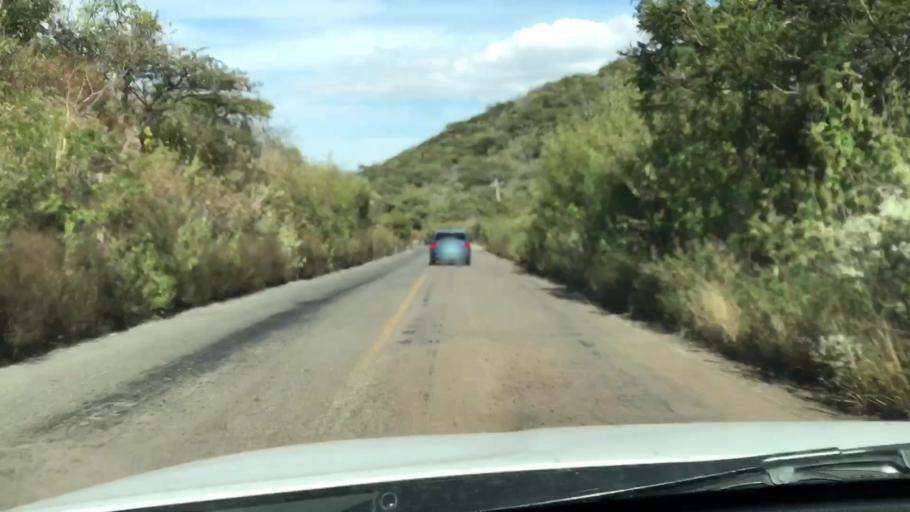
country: MX
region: Jalisco
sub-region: Zacoalco de Torres
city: Barranca de Otates (Barranca de Otatan)
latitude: 20.2251
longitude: -103.6903
